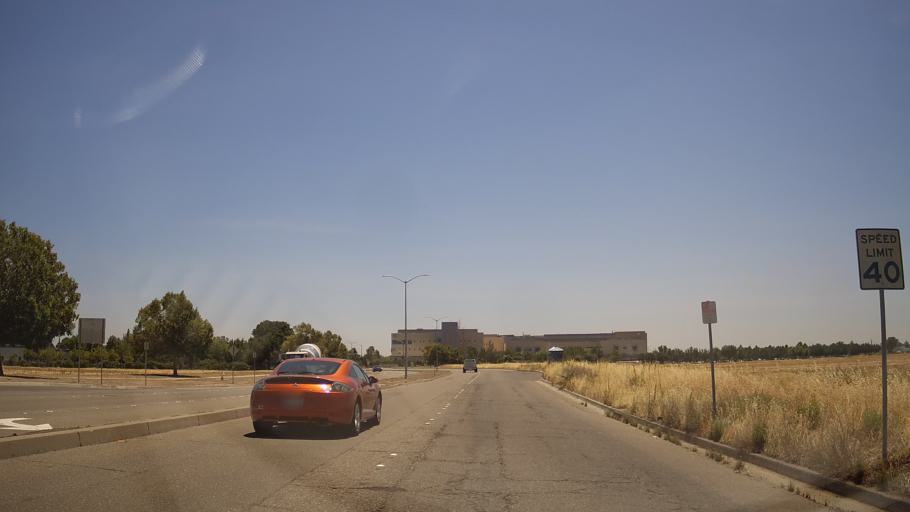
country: US
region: California
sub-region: Solano County
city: Hartley
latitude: 38.3919
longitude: -121.9430
